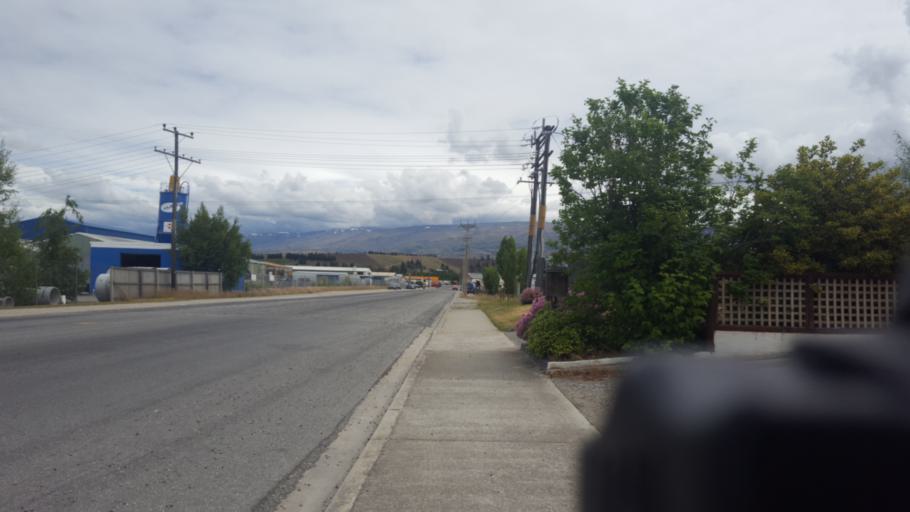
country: NZ
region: Otago
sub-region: Queenstown-Lakes District
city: Wanaka
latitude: -45.2462
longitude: 169.3758
